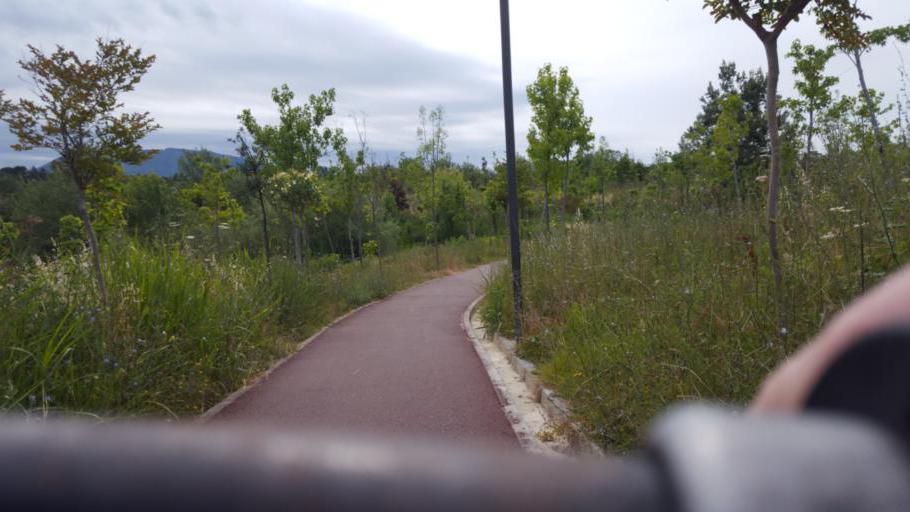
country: AL
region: Tirane
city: Tirana
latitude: 41.3064
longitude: 19.8203
